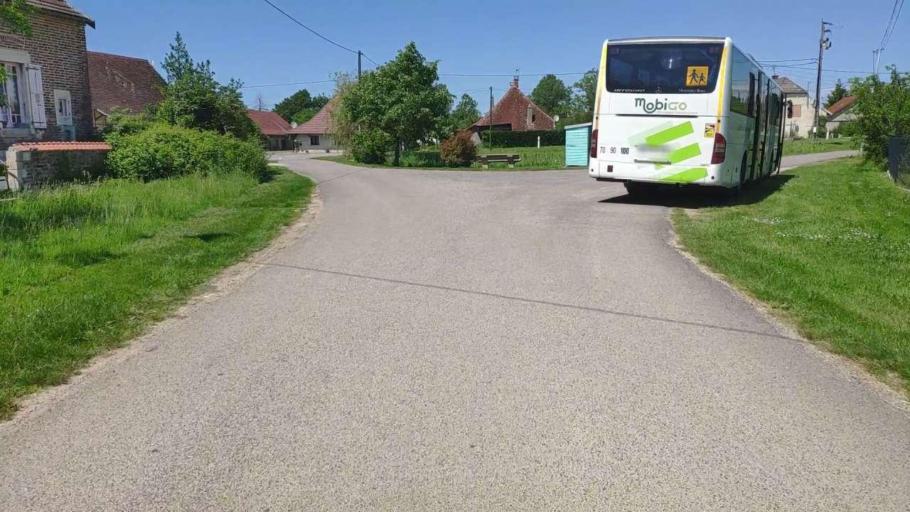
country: FR
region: Franche-Comte
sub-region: Departement du Jura
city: Bletterans
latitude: 46.7418
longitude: 5.3707
